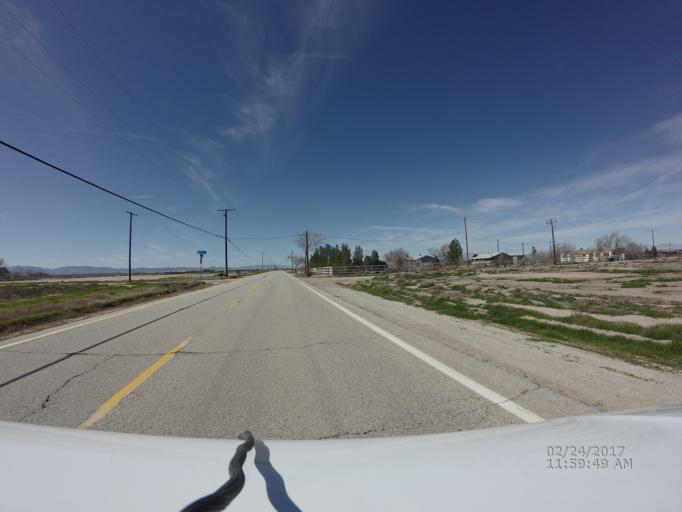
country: US
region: California
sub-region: Los Angeles County
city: Lancaster
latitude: 34.7193
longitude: -118.0140
